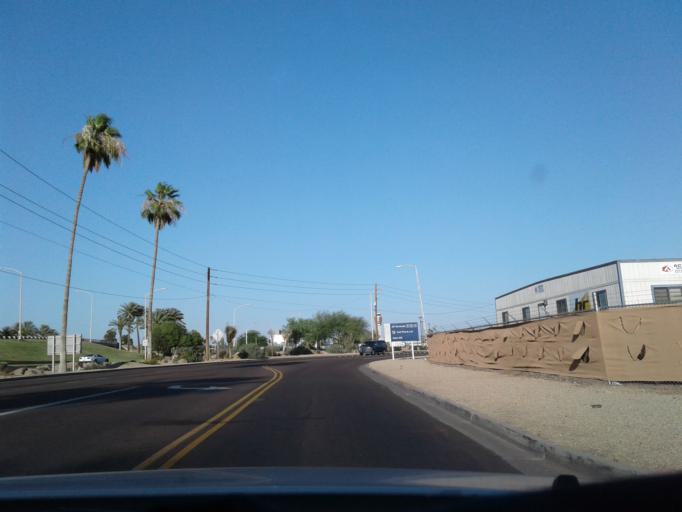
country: US
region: Arizona
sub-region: Maricopa County
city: Phoenix
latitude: 33.4367
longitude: -112.0238
